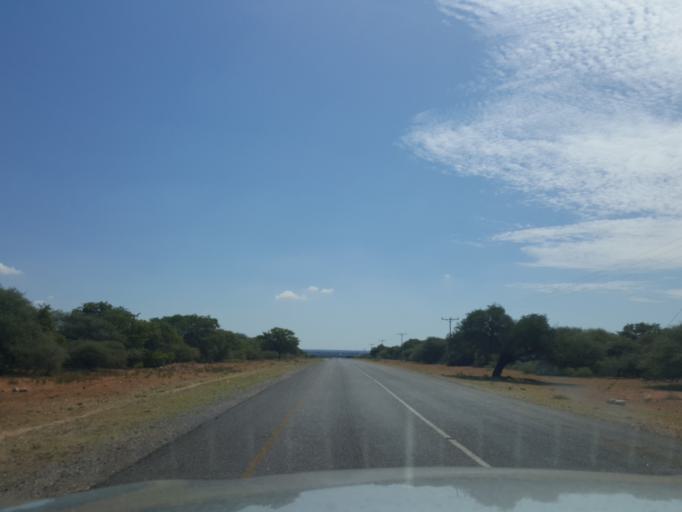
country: BW
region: Kweneng
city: Letlhakeng
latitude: -24.1225
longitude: 25.0891
